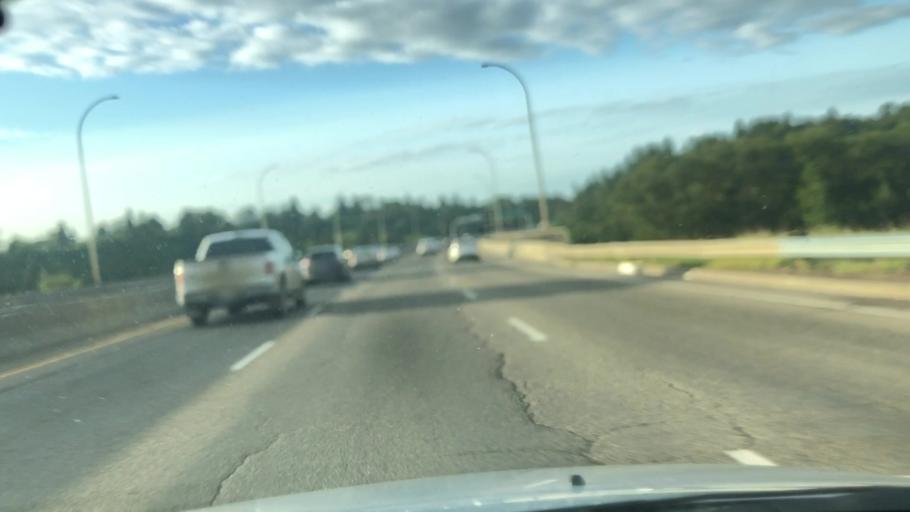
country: CA
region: Alberta
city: Edmonton
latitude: 53.5572
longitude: -113.4402
